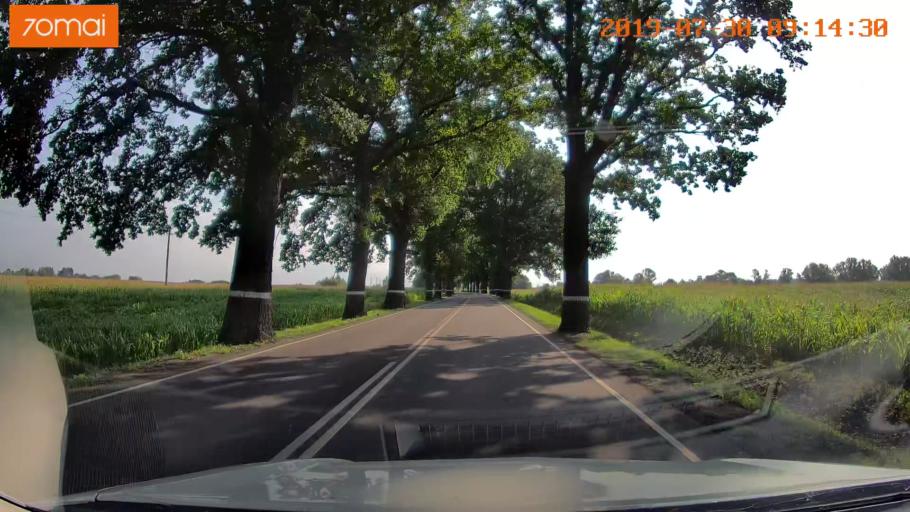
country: RU
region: Kaliningrad
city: Nesterov
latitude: 54.6294
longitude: 22.5195
